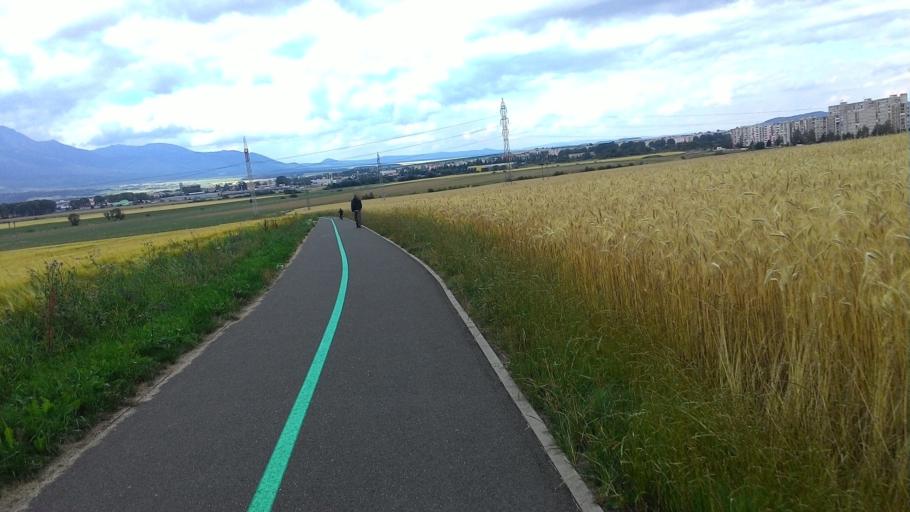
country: SK
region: Presovsky
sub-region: Okres Poprad
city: Poprad
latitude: 49.0394
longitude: 20.2712
